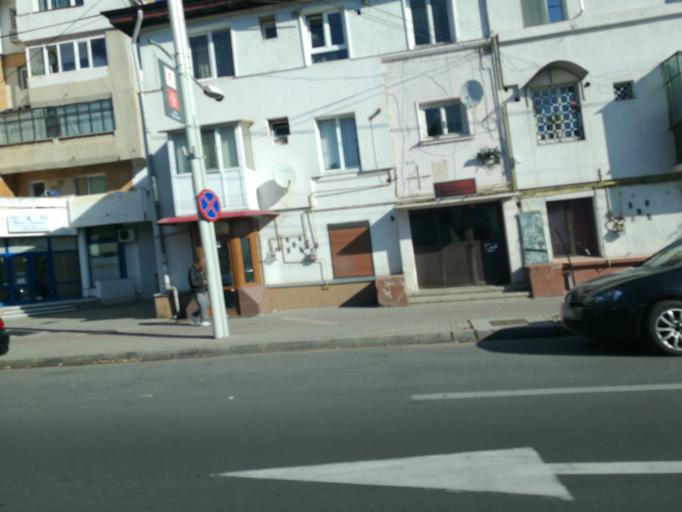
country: RO
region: Iasi
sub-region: Municipiul Iasi
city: Iasi
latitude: 47.1735
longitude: 27.5596
